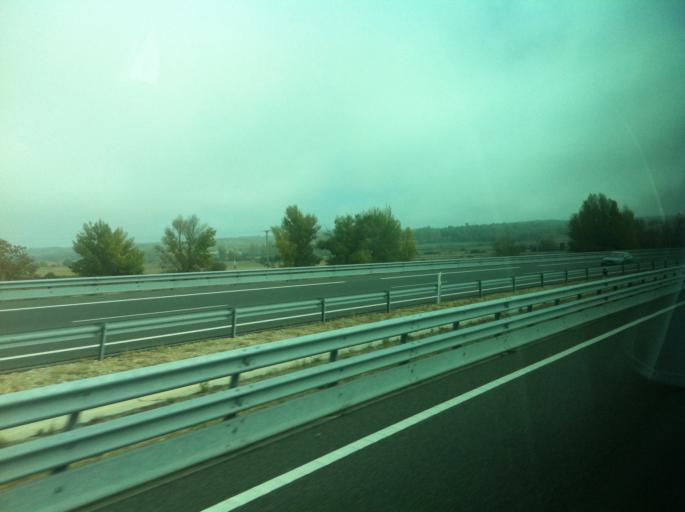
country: ES
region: Castille and Leon
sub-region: Provincia de Burgos
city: Quintana del Pidio
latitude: 41.7629
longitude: -3.6902
